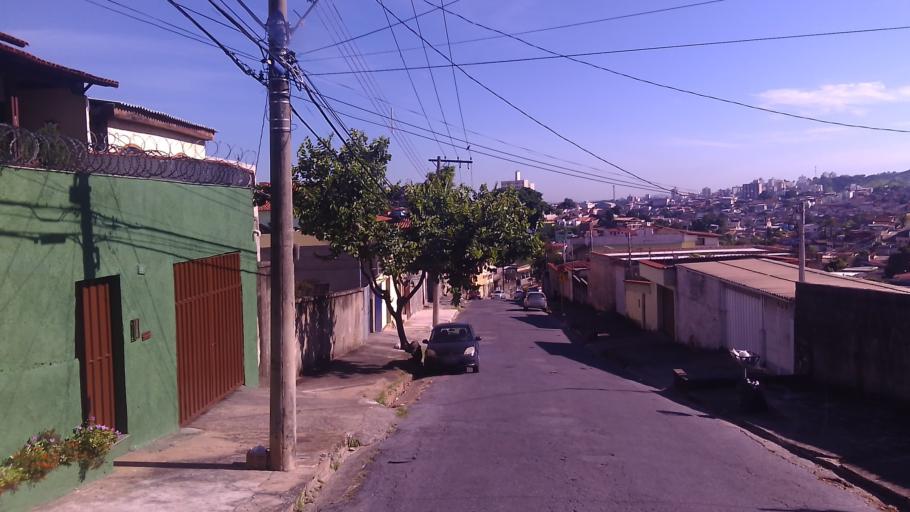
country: BR
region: Minas Gerais
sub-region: Contagem
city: Contagem
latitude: -19.9195
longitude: -44.0053
